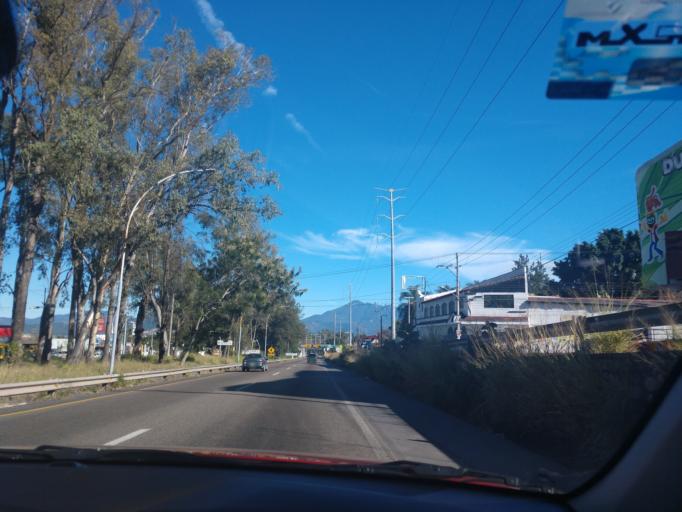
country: MX
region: Nayarit
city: Tepic
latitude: 21.5009
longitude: -104.9147
